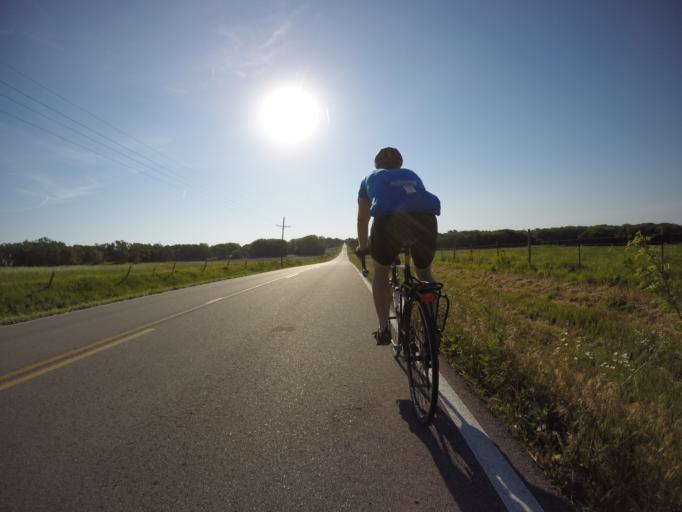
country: US
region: Nebraska
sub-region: Gage County
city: Wymore
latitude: 40.0884
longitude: -96.4919
